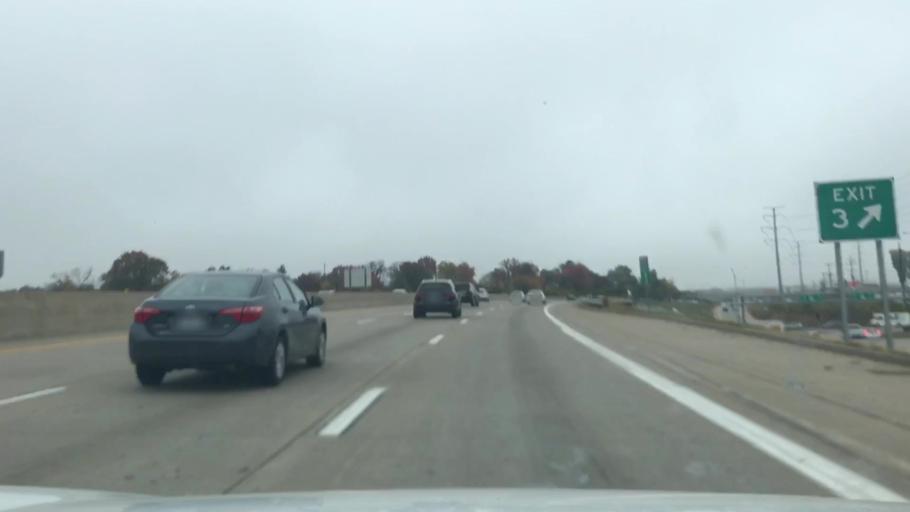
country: US
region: Missouri
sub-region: Saint Louis County
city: Olivette
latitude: 38.6723
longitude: -90.3621
